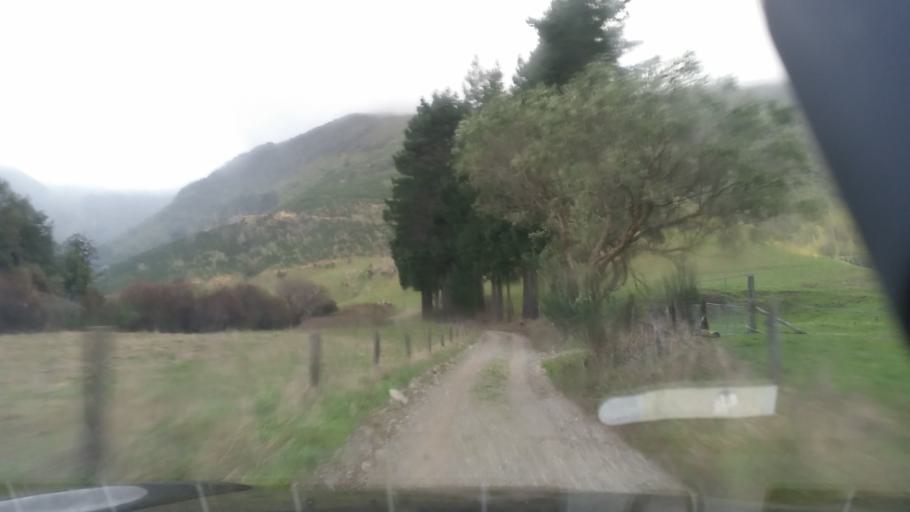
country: NZ
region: Marlborough
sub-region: Marlborough District
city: Picton
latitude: -41.2153
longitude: 173.6970
